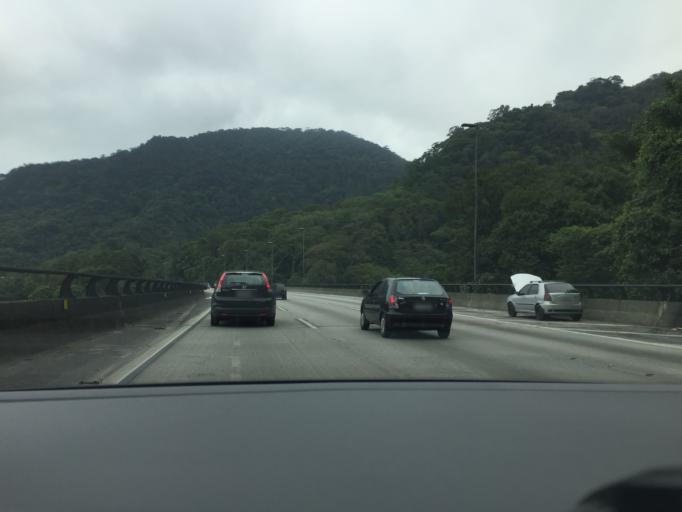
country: BR
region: Sao Paulo
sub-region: Cubatao
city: Cubatao
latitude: -23.8949
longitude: -46.5059
